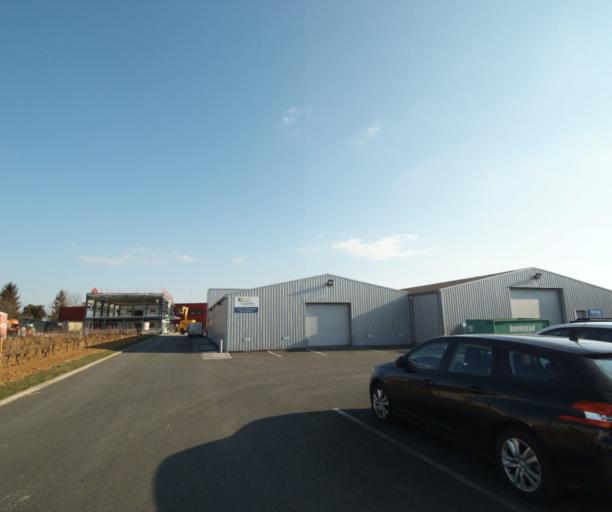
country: FR
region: Poitou-Charentes
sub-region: Departement des Deux-Sevres
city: Niort
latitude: 46.3384
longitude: -0.4202
